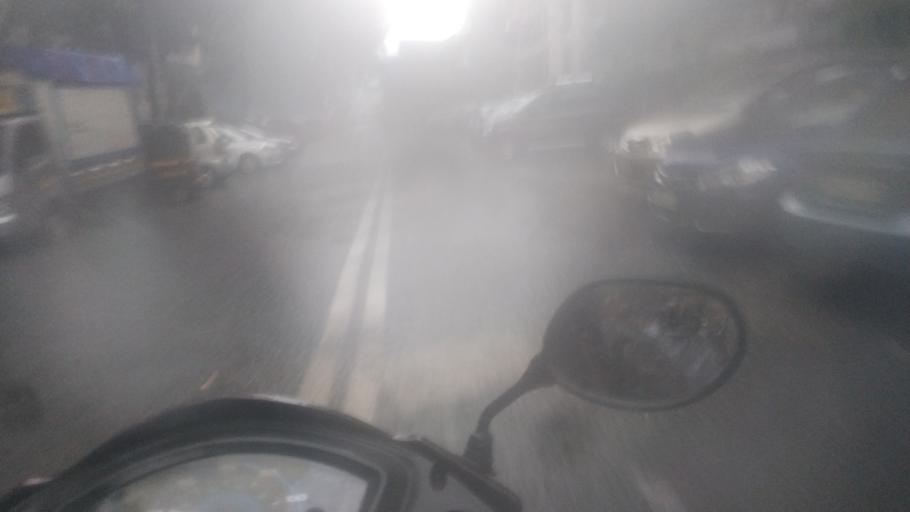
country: IN
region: Maharashtra
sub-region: Mumbai Suburban
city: Mumbai
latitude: 19.1152
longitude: 72.8368
